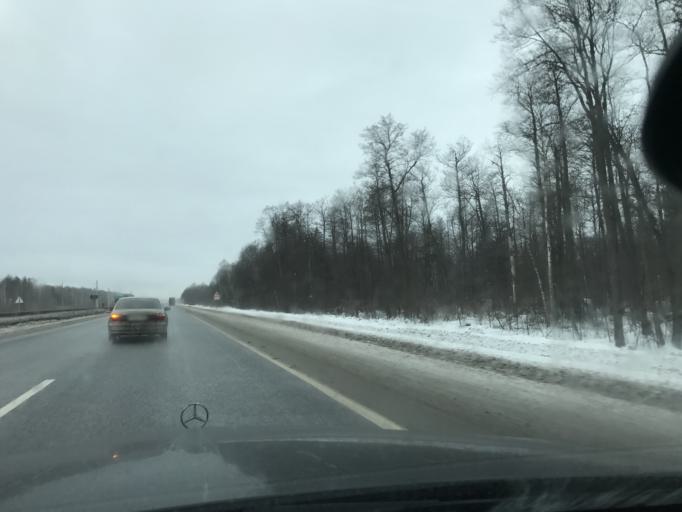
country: RU
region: Nizjnij Novgorod
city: Volodarsk
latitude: 56.2849
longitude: 43.1621
